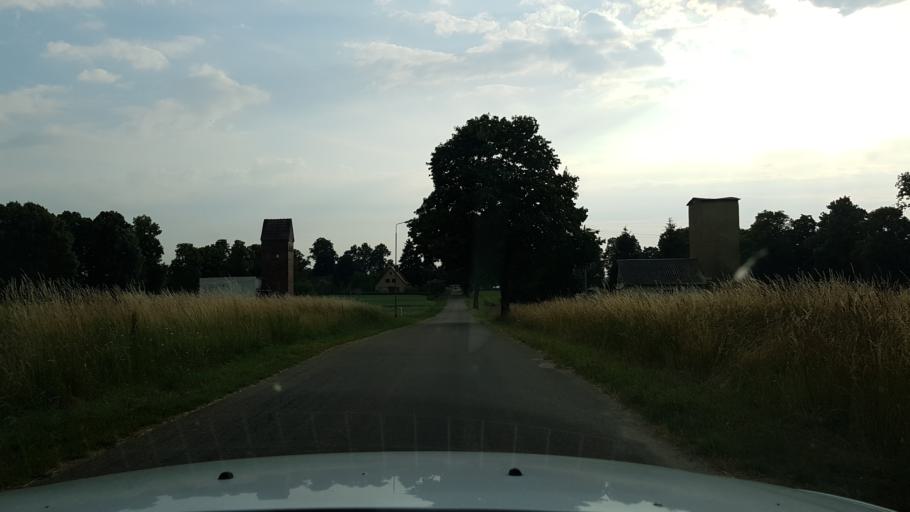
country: PL
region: West Pomeranian Voivodeship
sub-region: Powiat swidwinski
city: Swidwin
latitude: 53.8112
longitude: 15.8638
